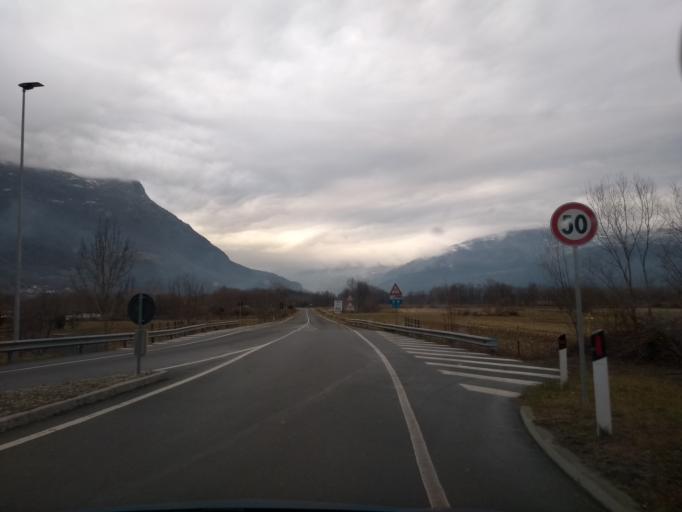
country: IT
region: Piedmont
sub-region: Provincia di Torino
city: Fiorano Canavese
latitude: 45.4796
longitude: 7.8307
